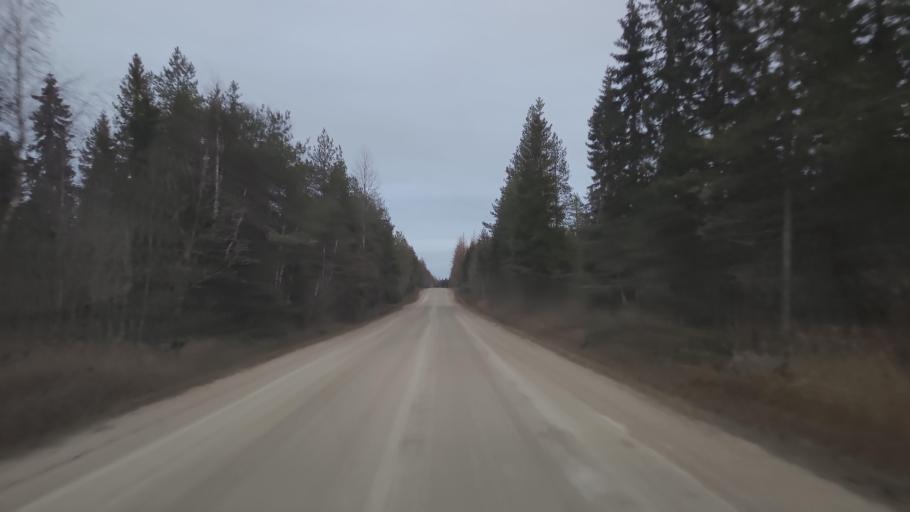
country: FI
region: Lapland
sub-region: Kemi-Tornio
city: Tervola
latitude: 66.0716
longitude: 24.8735
